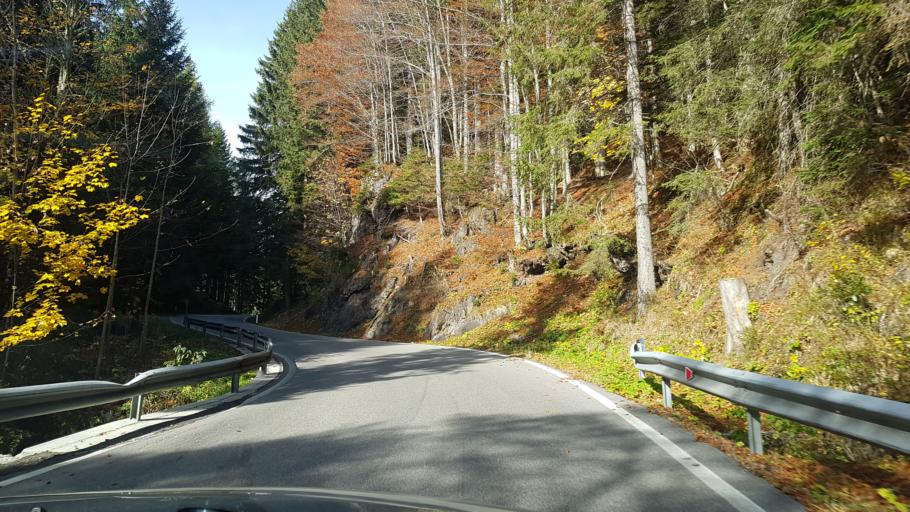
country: IT
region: Veneto
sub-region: Provincia di Belluno
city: Candide
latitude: 46.6440
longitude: 12.4535
